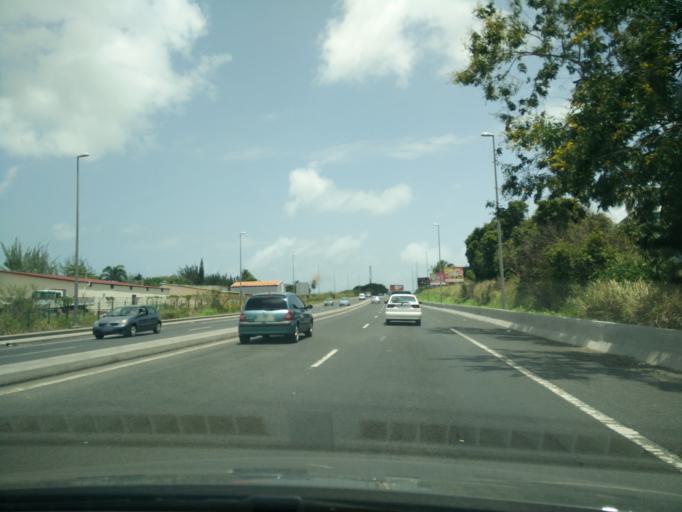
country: GP
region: Guadeloupe
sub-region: Guadeloupe
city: Baie-Mahault
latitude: 16.2604
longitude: -61.5709
